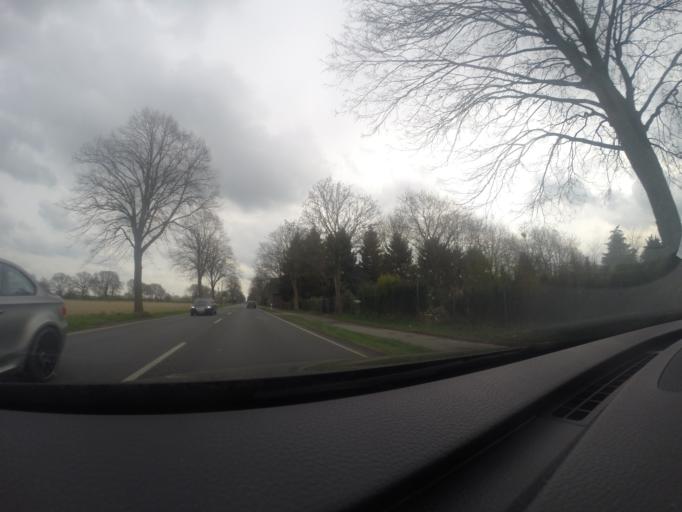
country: DE
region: North Rhine-Westphalia
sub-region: Regierungsbezirk Dusseldorf
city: Alpen
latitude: 51.5861
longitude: 6.5473
